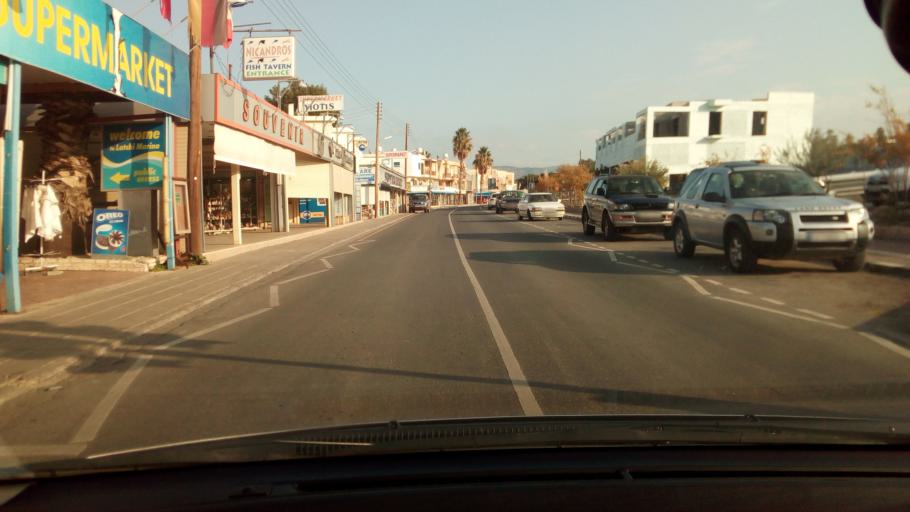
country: CY
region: Pafos
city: Polis
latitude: 35.0405
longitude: 32.3943
